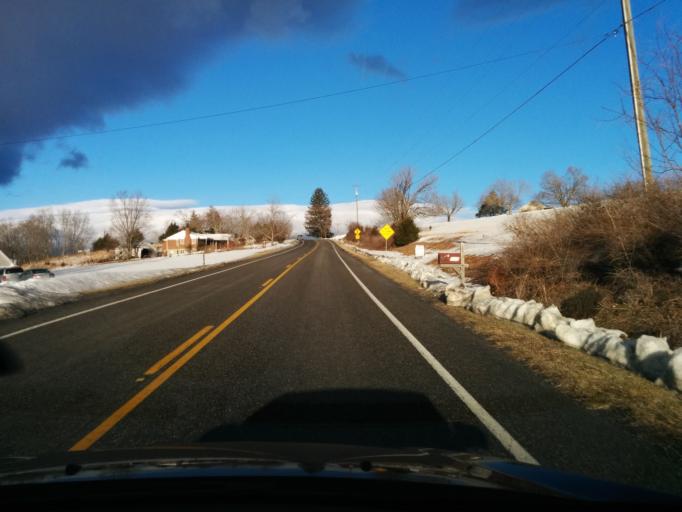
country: US
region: Virginia
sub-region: City of Lexington
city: Lexington
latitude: 37.7562
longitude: -79.4765
